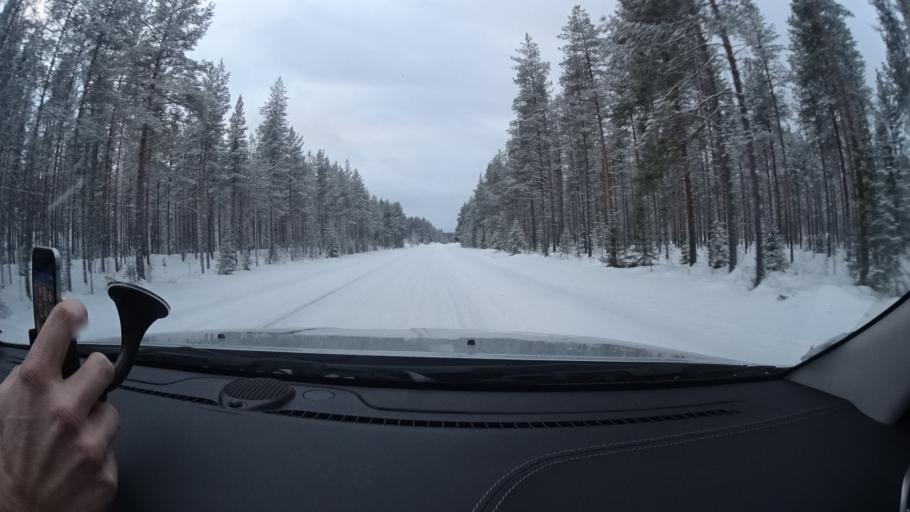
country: FI
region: Lapland
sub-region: Itae-Lappi
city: Kemijaervi
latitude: 66.3311
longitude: 27.0448
